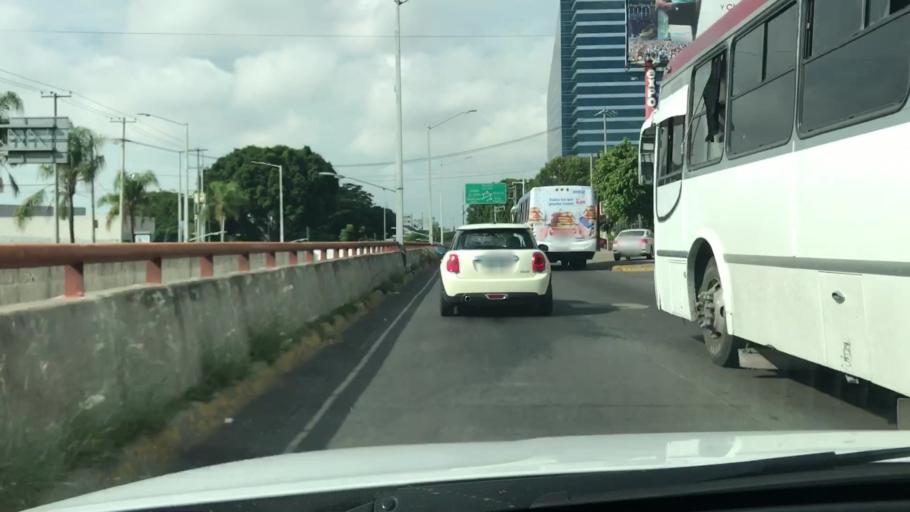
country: MX
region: Jalisco
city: Guadalajara
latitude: 20.6679
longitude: -103.3918
